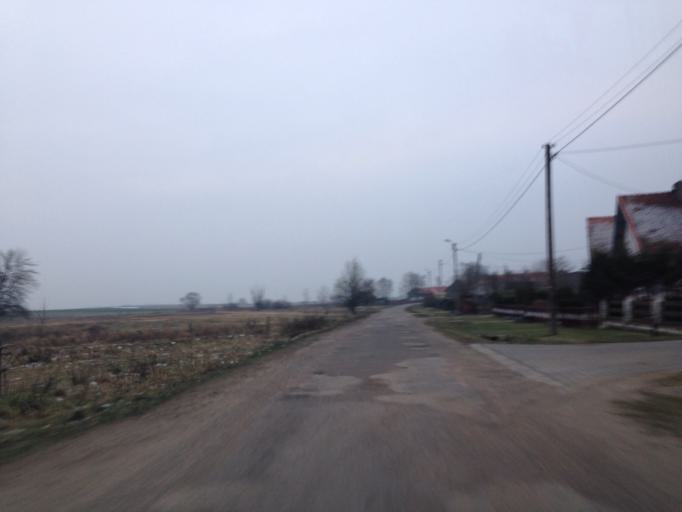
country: PL
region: Warmian-Masurian Voivodeship
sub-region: Powiat ketrzynski
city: Korsze
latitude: 54.2698
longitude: 21.1429
